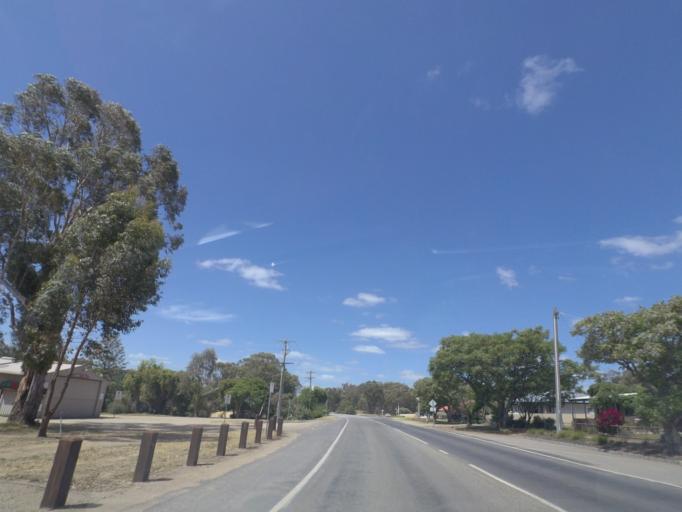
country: AU
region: Victoria
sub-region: Wangaratta
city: Wangaratta
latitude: -36.4635
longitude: 146.2255
